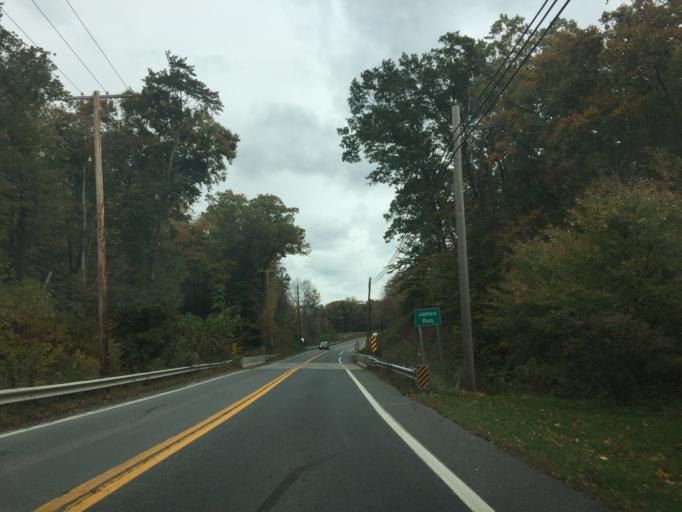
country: US
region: Maryland
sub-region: Harford County
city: Riverside
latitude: 39.5291
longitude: -76.2628
